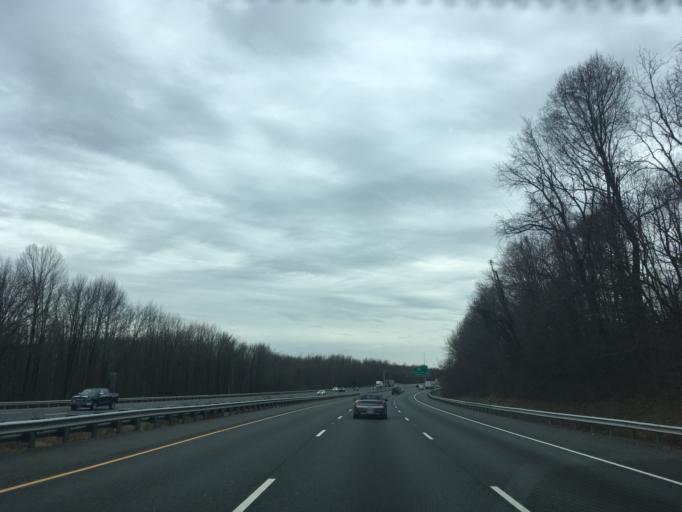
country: US
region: Maryland
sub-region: Harford County
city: Aberdeen
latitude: 39.5333
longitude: -76.1768
